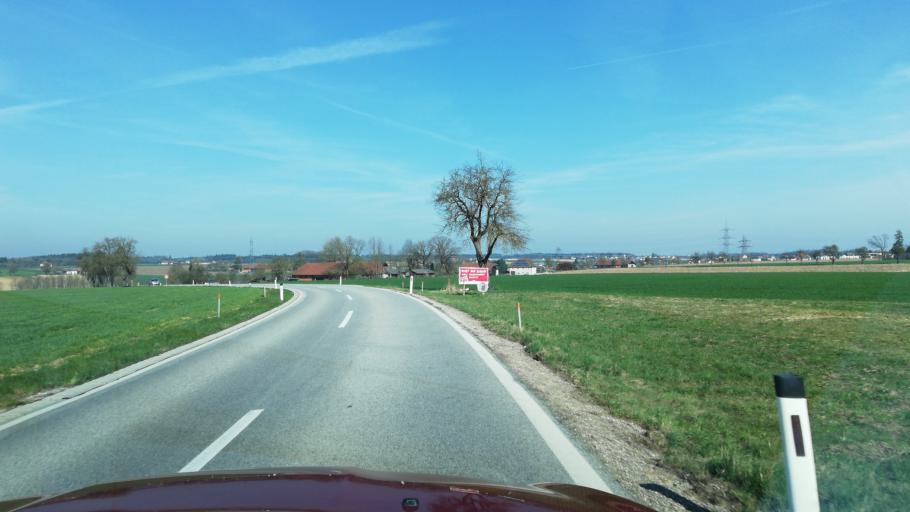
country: AT
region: Upper Austria
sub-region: Politischer Bezirk Kirchdorf an der Krems
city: Kremsmunster
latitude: 48.0851
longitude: 14.1125
